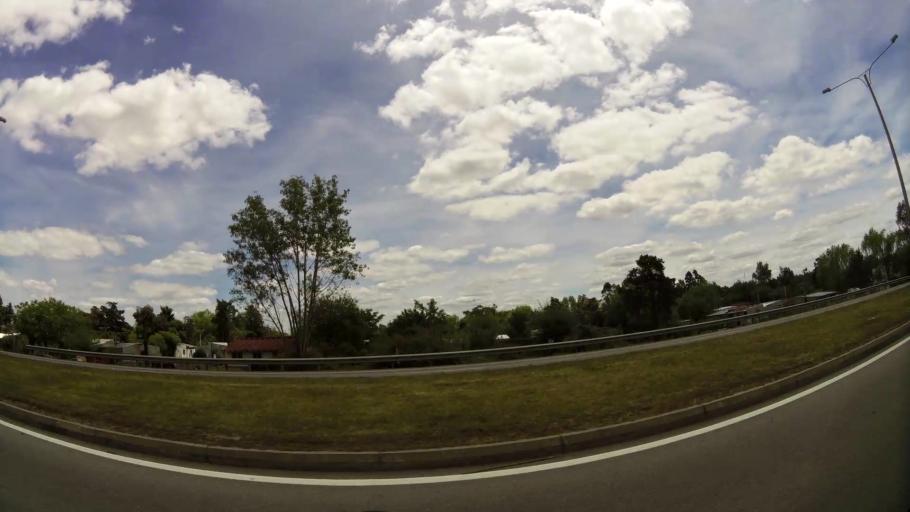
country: UY
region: Canelones
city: Pando
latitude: -34.8047
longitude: -55.9562
